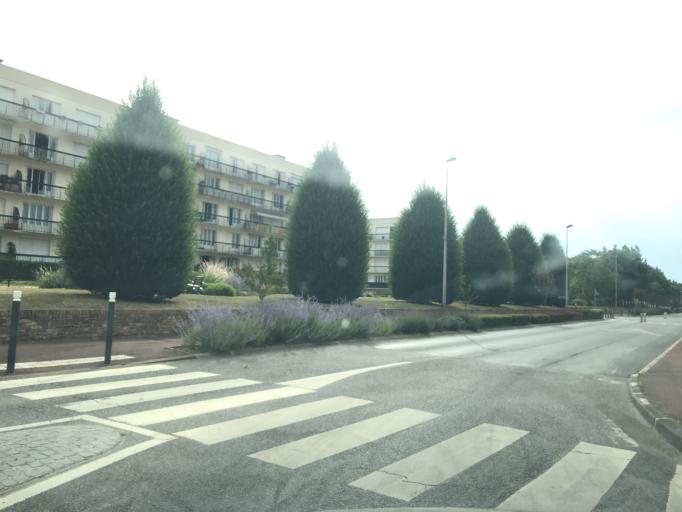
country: FR
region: Ile-de-France
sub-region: Departement des Yvelines
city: Maurepas
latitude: 48.7647
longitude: 1.9351
